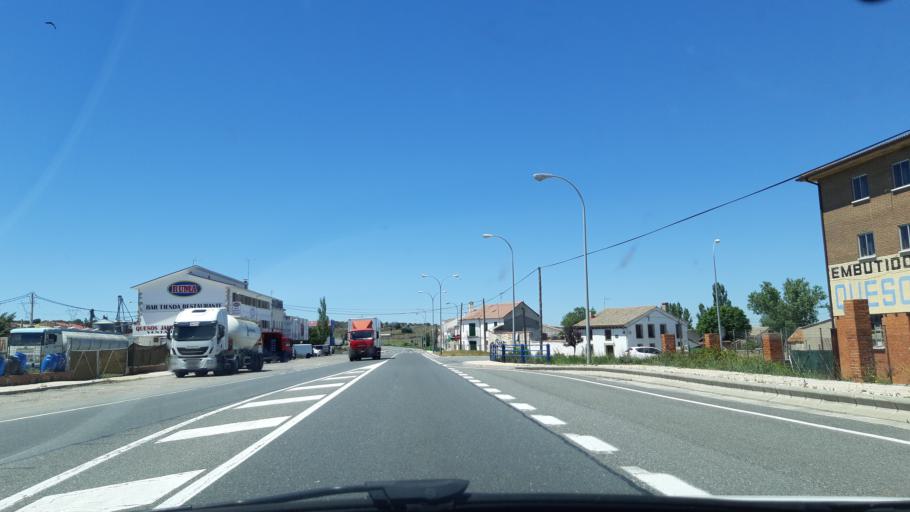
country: ES
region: Castille and Leon
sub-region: Provincia de Segovia
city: Zarzuela del Monte
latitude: 40.7572
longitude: -4.3304
